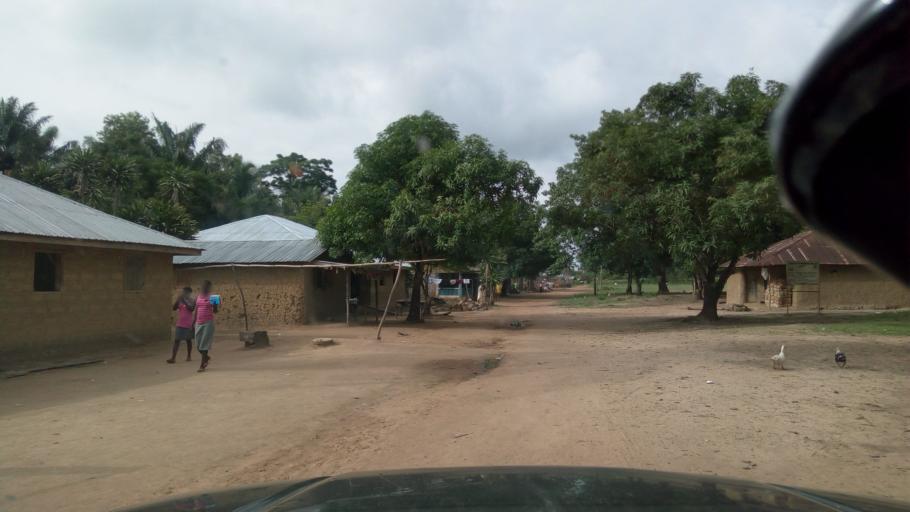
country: SL
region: Northern Province
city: Lunsar
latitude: 8.8177
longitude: -12.5819
